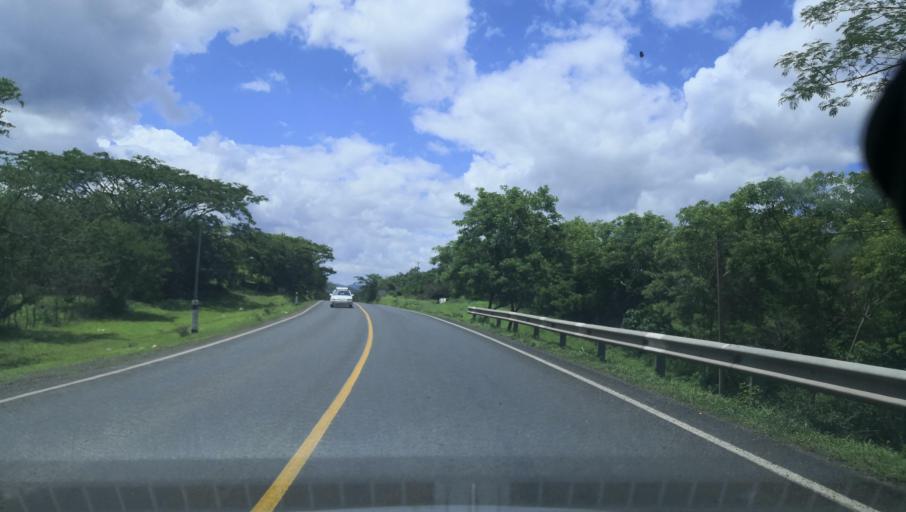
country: NI
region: Esteli
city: Condega
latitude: 13.3958
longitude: -86.3996
